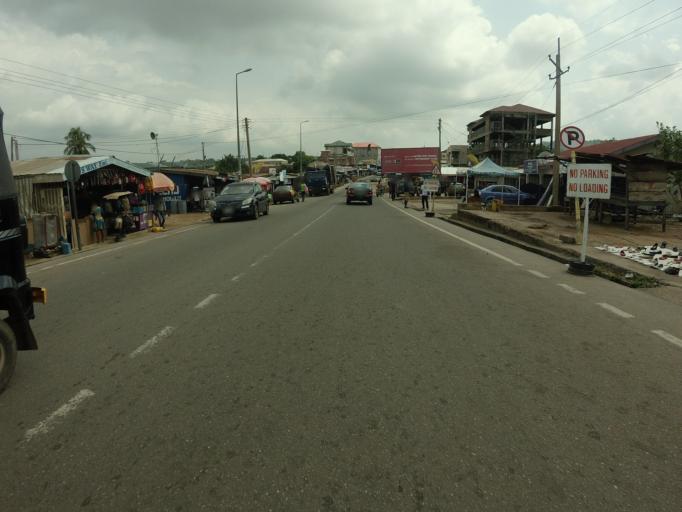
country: GH
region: Volta
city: Ho
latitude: 6.6190
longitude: 0.4703
